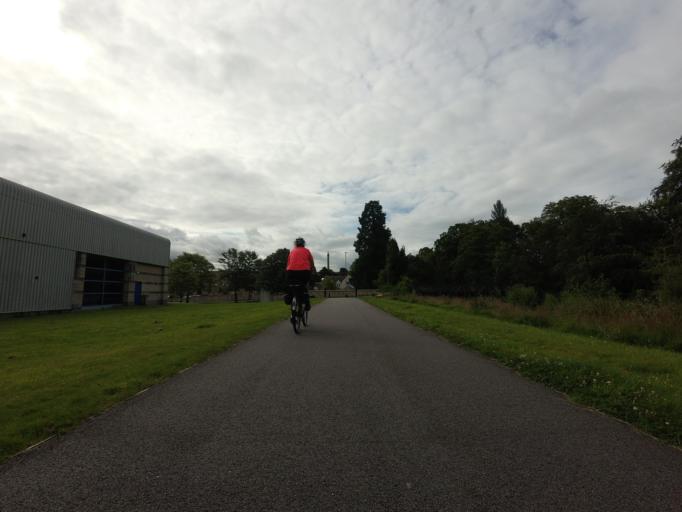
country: GB
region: Scotland
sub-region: Moray
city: Elgin
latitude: 57.6516
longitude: -3.3250
